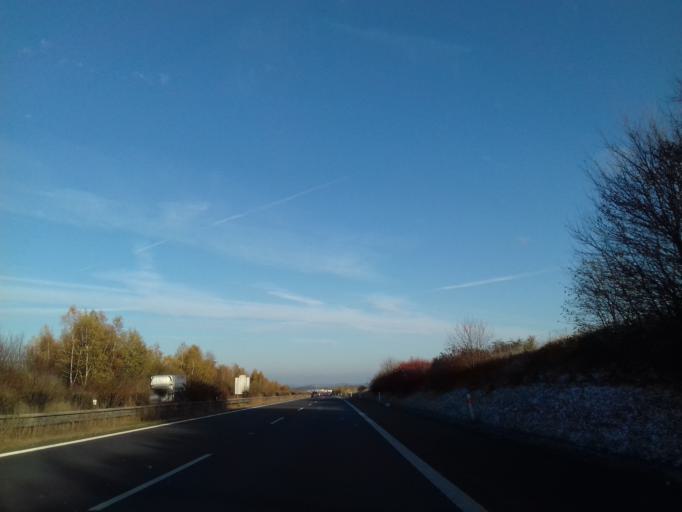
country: CZ
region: Central Bohemia
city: Komarov
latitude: 49.8419
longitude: 13.8262
